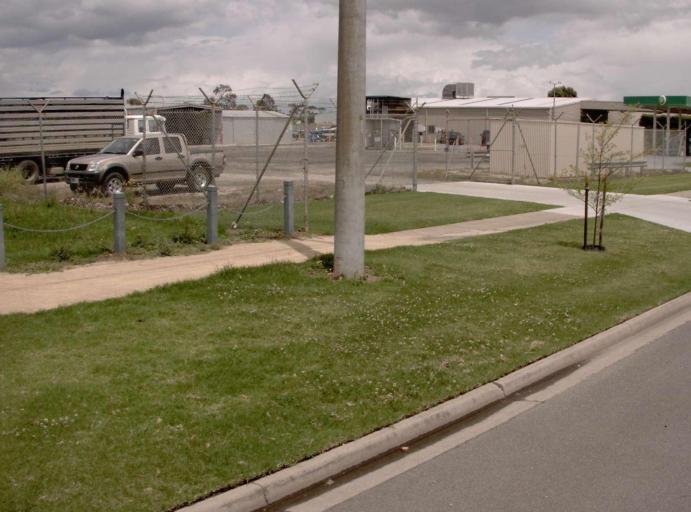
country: AU
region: Victoria
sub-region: Wellington
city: Sale
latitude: -38.1016
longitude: 147.0931
